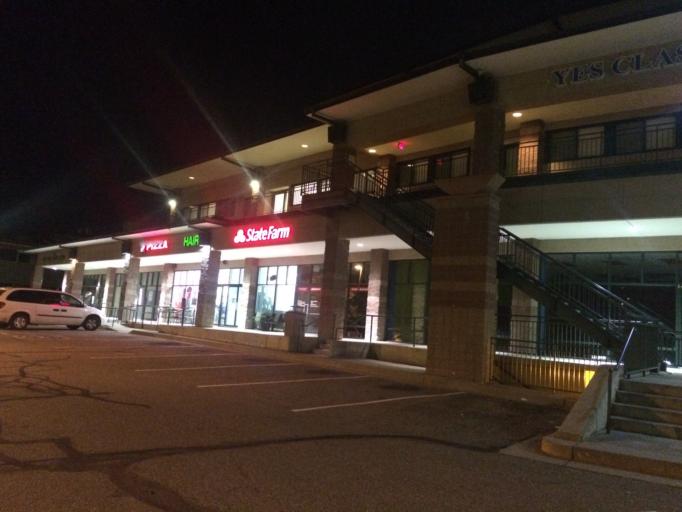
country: US
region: Colorado
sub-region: Boulder County
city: Louisville
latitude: 39.9874
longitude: -105.1296
